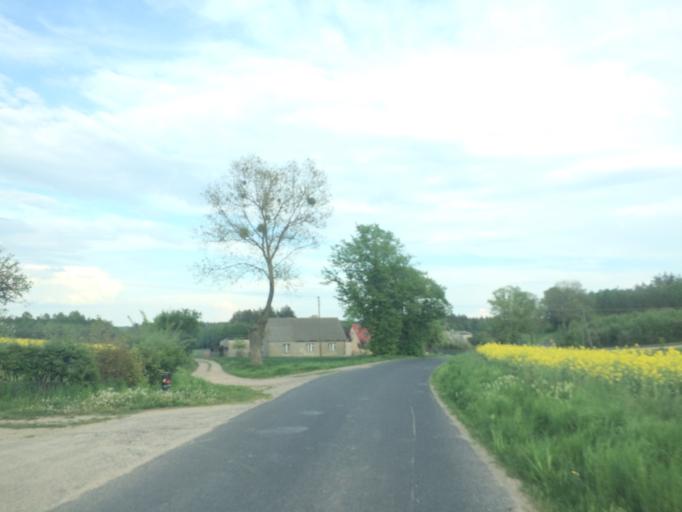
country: PL
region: Warmian-Masurian Voivodeship
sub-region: Powiat nowomiejski
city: Nowe Miasto Lubawskie
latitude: 53.4193
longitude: 19.6807
